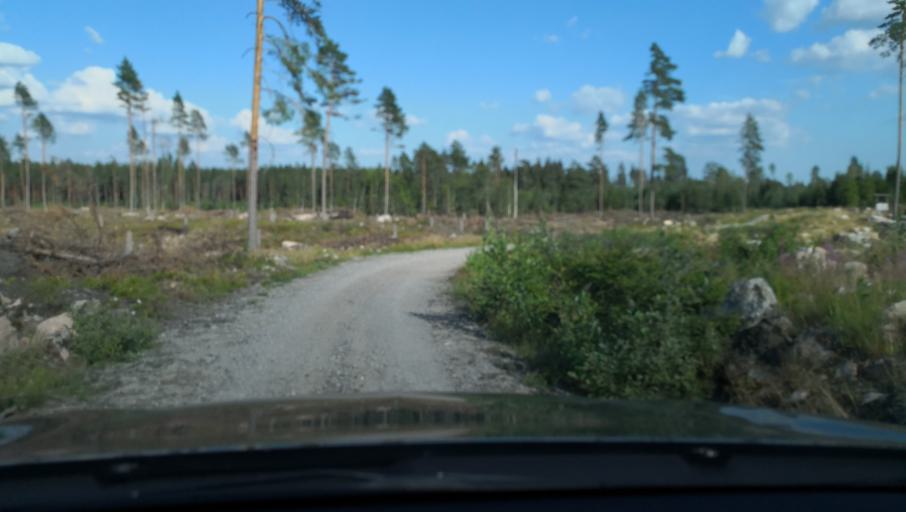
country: SE
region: Vaestmanland
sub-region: Vasteras
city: Skultuna
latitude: 59.7084
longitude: 16.3853
